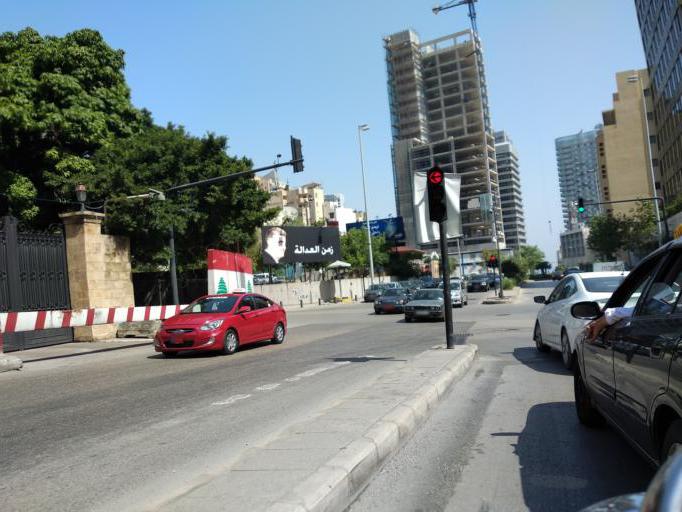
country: LB
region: Beyrouth
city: Beirut
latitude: 33.8955
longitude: 35.4960
